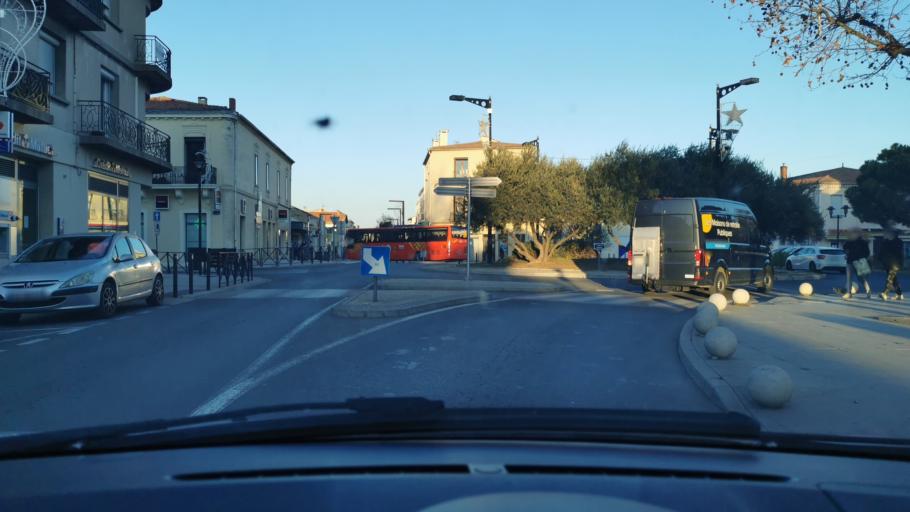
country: FR
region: Languedoc-Roussillon
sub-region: Departement de l'Herault
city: Frontignan
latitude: 43.4476
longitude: 3.7549
